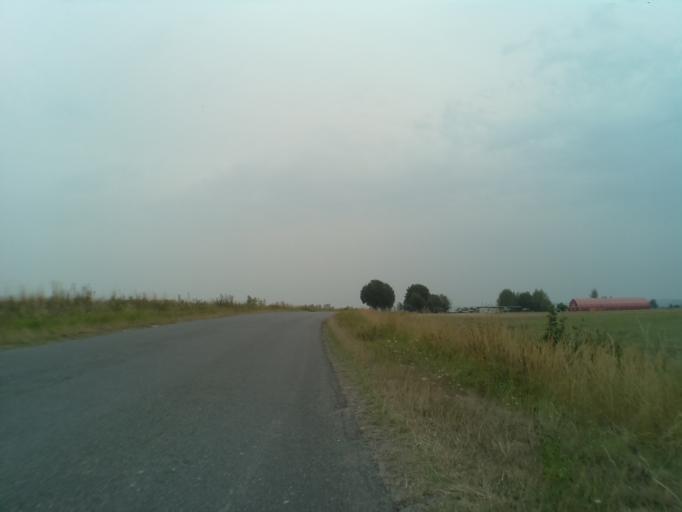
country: PL
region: Lower Silesian Voivodeship
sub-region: Powiat swidnicki
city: Swiebodzice
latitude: 50.8852
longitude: 16.3233
